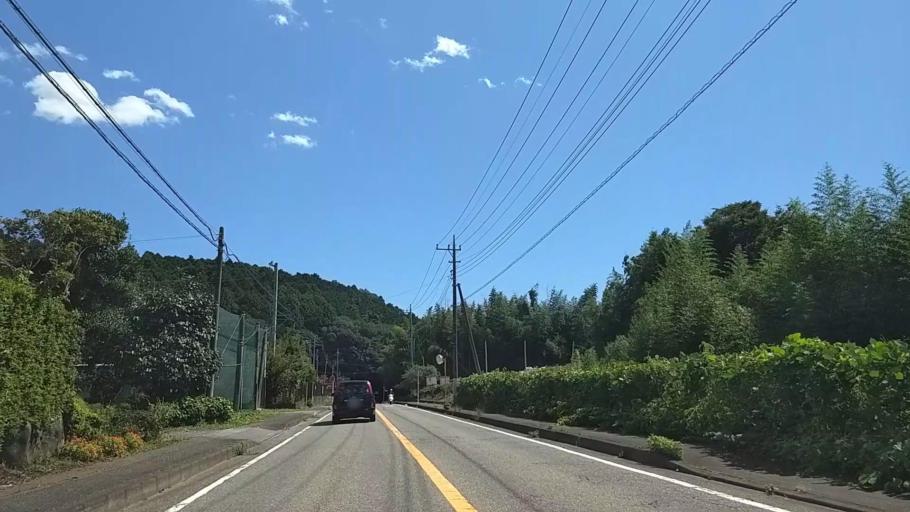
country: JP
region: Kanagawa
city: Zama
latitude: 35.5477
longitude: 139.2976
